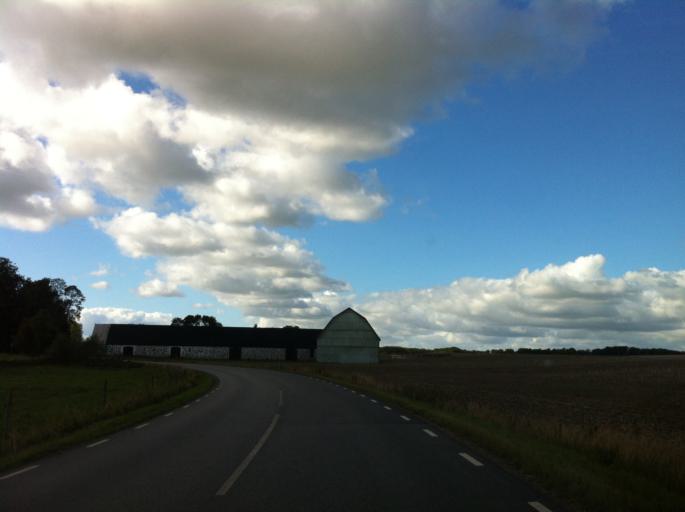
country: SE
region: Skane
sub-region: Tomelilla Kommun
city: Tomelilla
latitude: 55.6492
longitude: 13.9632
